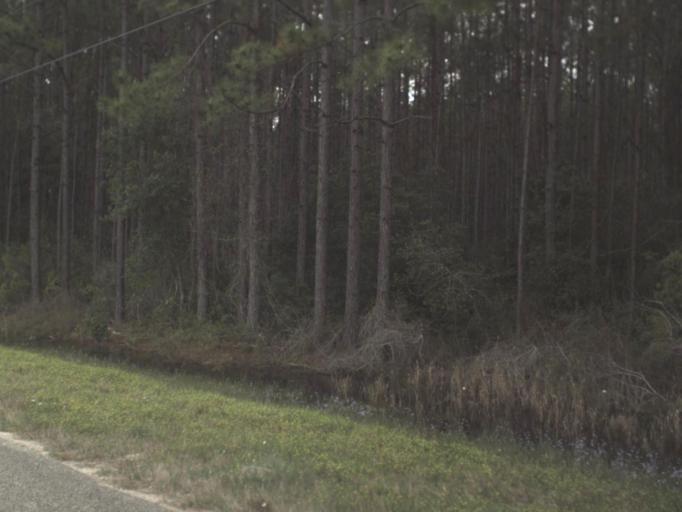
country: US
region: Florida
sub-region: Gulf County
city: Port Saint Joe
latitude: 29.8366
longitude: -85.2740
